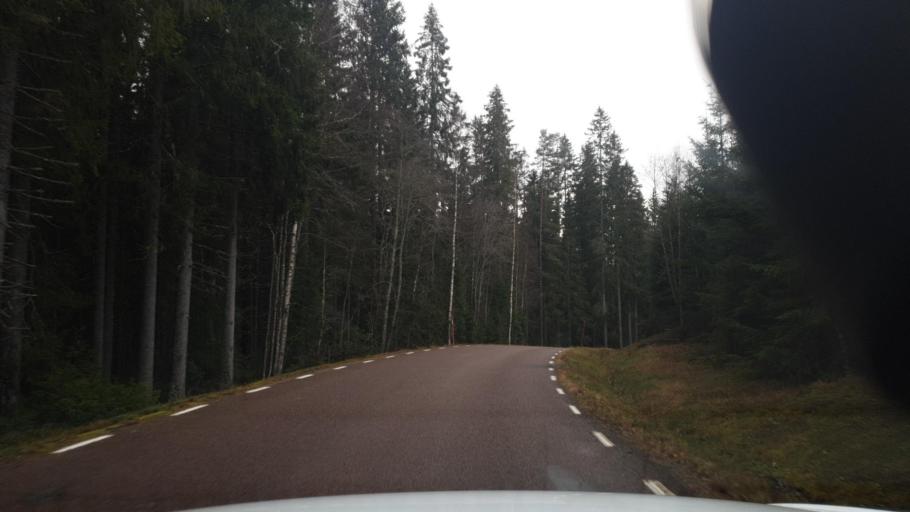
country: SE
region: Vaermland
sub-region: Arvika Kommun
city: Arvika
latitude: 59.7935
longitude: 12.8393
